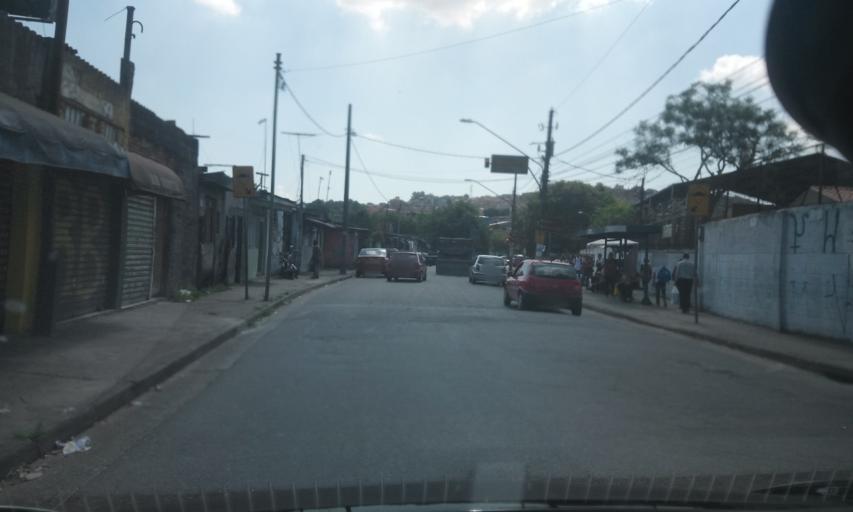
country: BR
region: Sao Paulo
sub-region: Sao Bernardo Do Campo
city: Sao Bernardo do Campo
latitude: -23.7108
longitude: -46.5302
